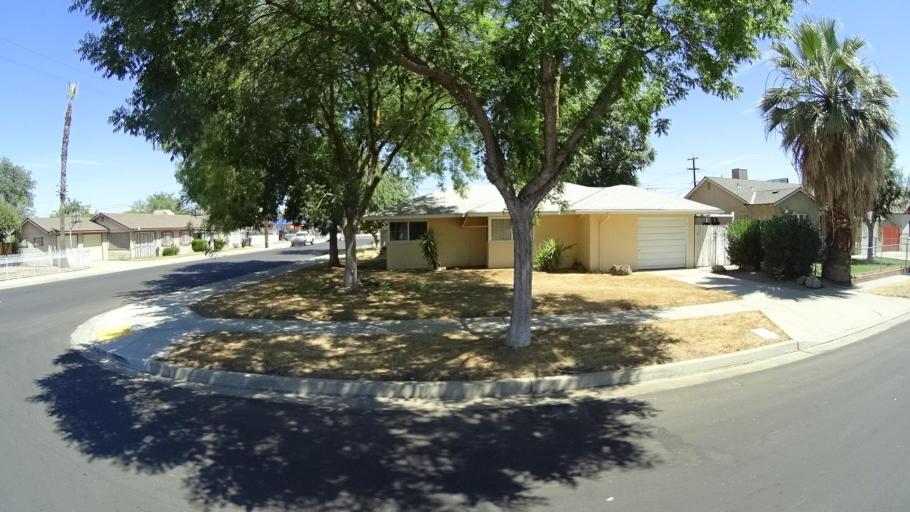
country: US
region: California
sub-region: Fresno County
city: Fresno
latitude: 36.7495
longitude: -119.7385
